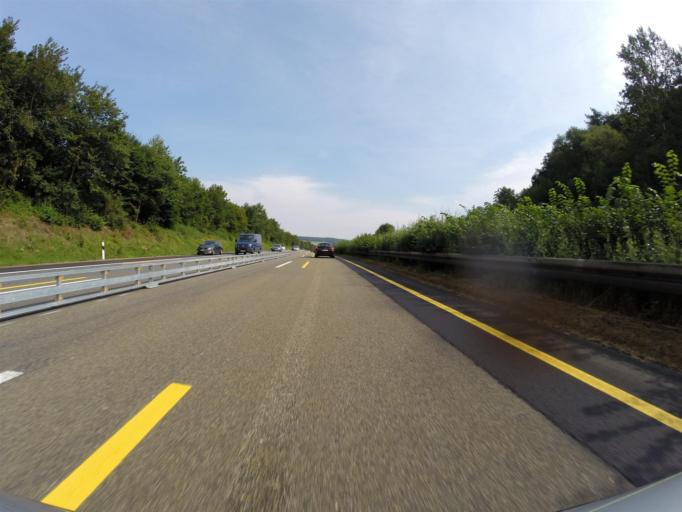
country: DE
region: Hesse
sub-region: Regierungsbezirk Kassel
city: Homberg
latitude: 51.0031
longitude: 9.4797
